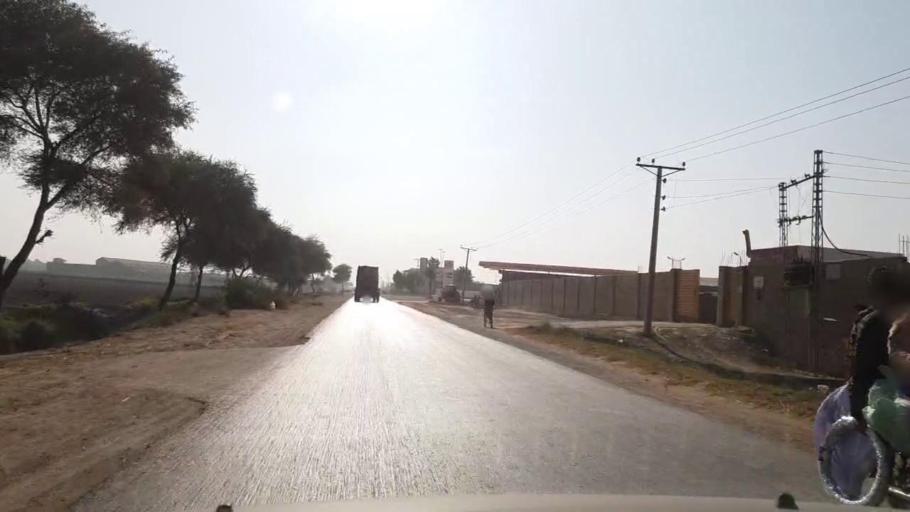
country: PK
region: Sindh
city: Tando Muhammad Khan
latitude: 25.1086
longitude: 68.5208
